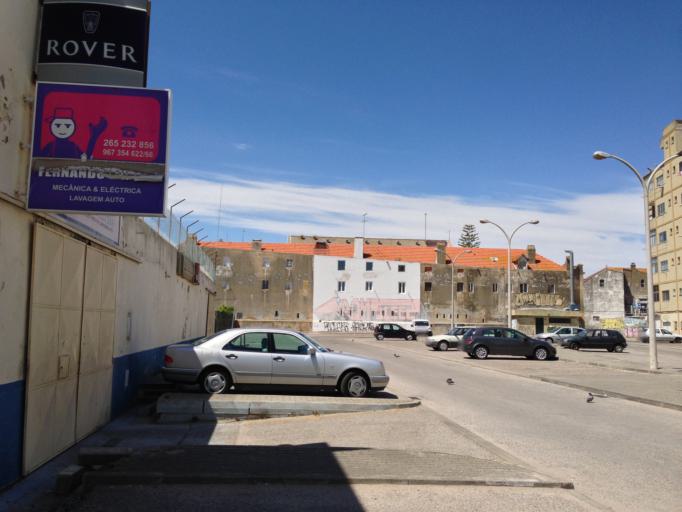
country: PT
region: Setubal
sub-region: Setubal
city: Setubal
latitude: 38.5218
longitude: -8.8953
